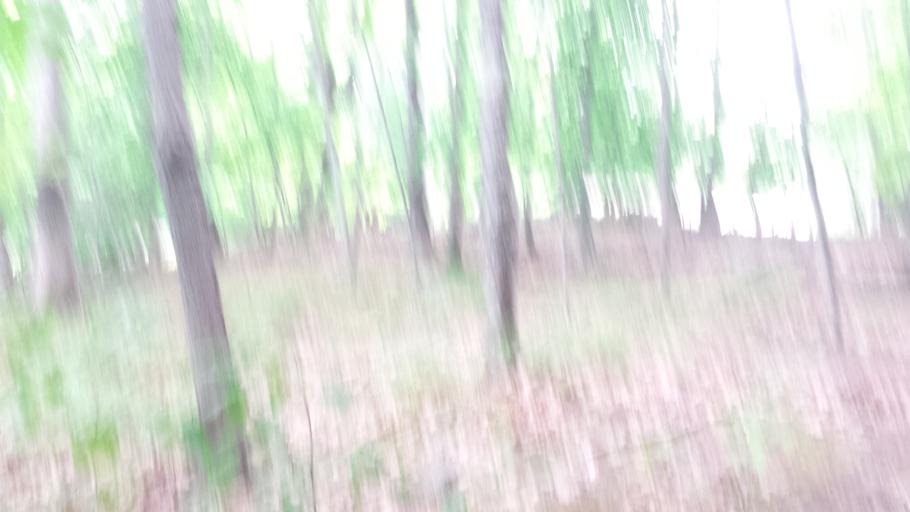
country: US
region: New York
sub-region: Putnam County
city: Peach Lake
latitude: 41.3096
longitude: -73.5702
